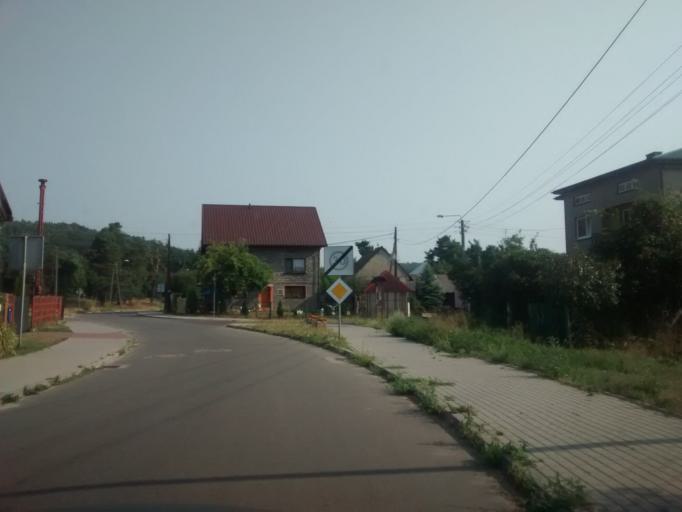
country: PL
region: Silesian Voivodeship
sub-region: Powiat zawiercianski
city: Kroczyce
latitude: 50.5647
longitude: 19.5344
